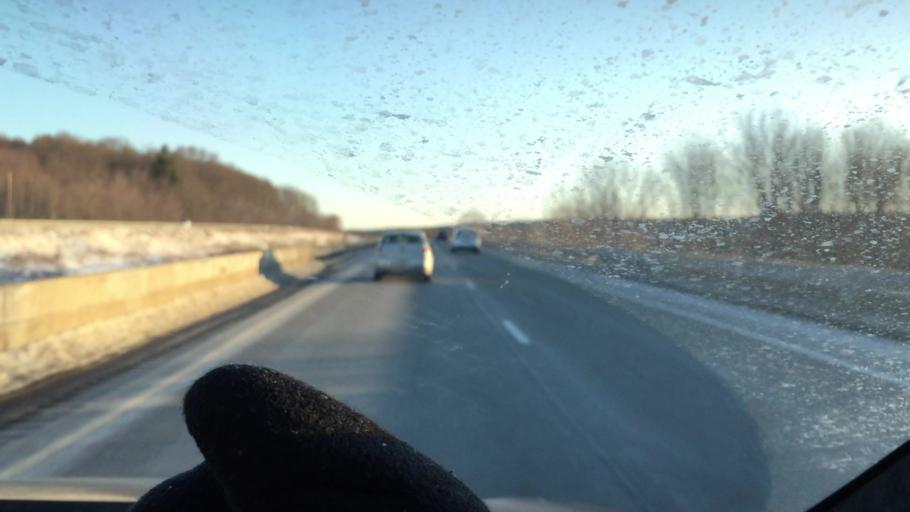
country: US
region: Pennsylvania
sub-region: Crawford County
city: Meadville
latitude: 41.6829
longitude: -80.2070
